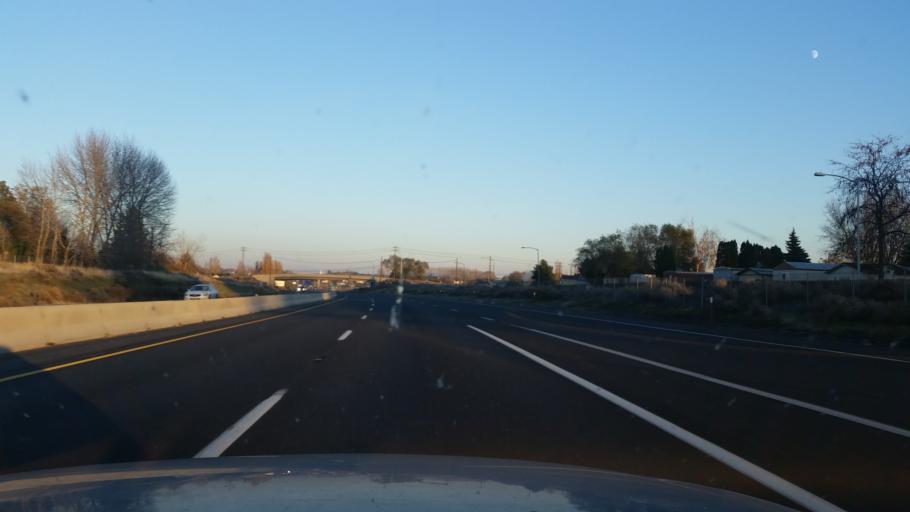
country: US
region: Washington
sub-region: Grant County
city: Cascade Valley
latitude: 47.1004
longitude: -119.3111
